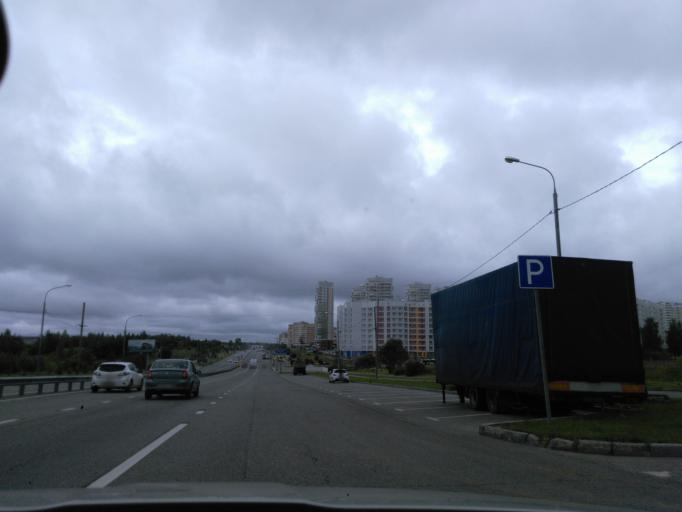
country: RU
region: Moscow
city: Zelenograd
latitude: 55.9703
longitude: 37.1801
